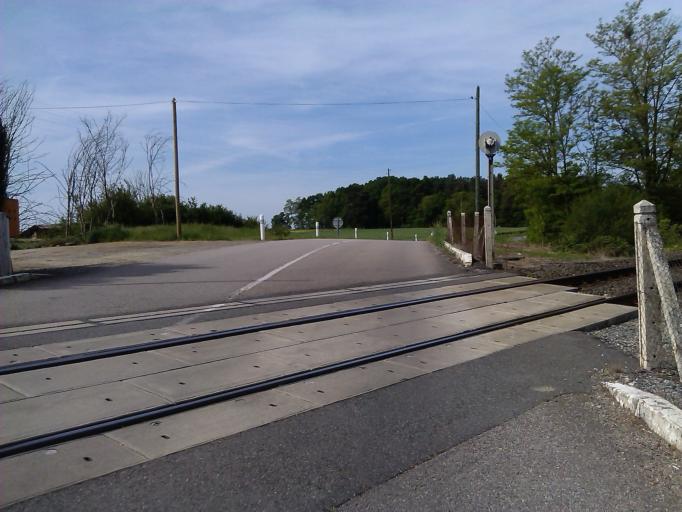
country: FR
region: Auvergne
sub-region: Departement de l'Allier
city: Dompierre-sur-Besbre
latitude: 46.5245
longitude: 3.6086
